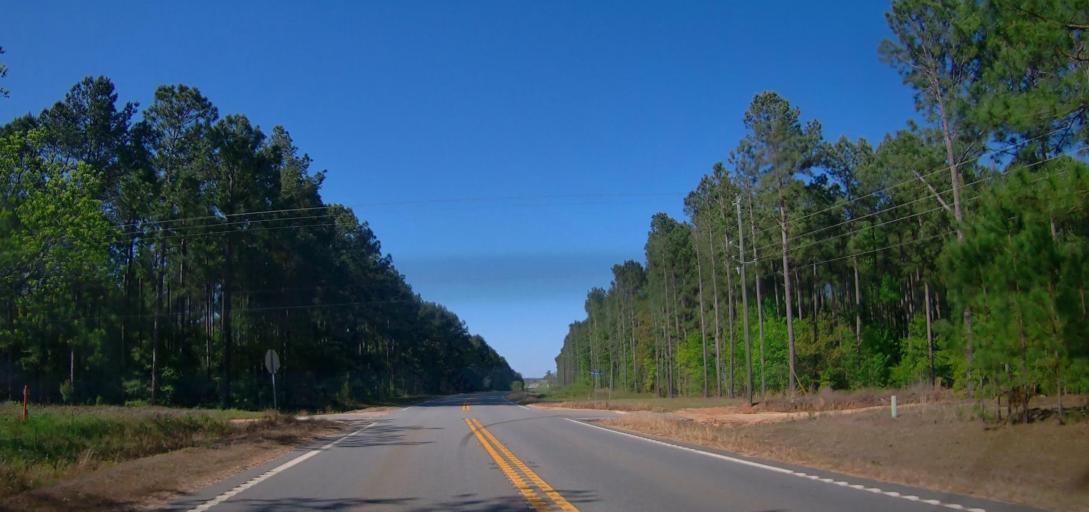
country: US
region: Georgia
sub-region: Pulaski County
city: Hawkinsville
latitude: 32.1664
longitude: -83.5119
